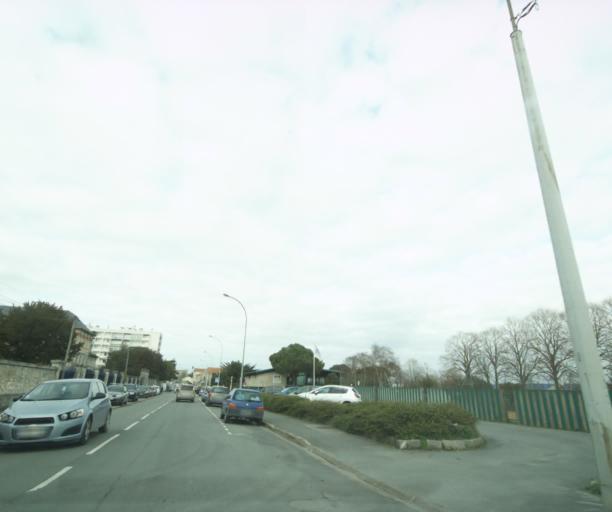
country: FR
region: Poitou-Charentes
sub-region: Departement de la Charente-Maritime
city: La Rochelle
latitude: 46.1654
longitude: -1.1645
